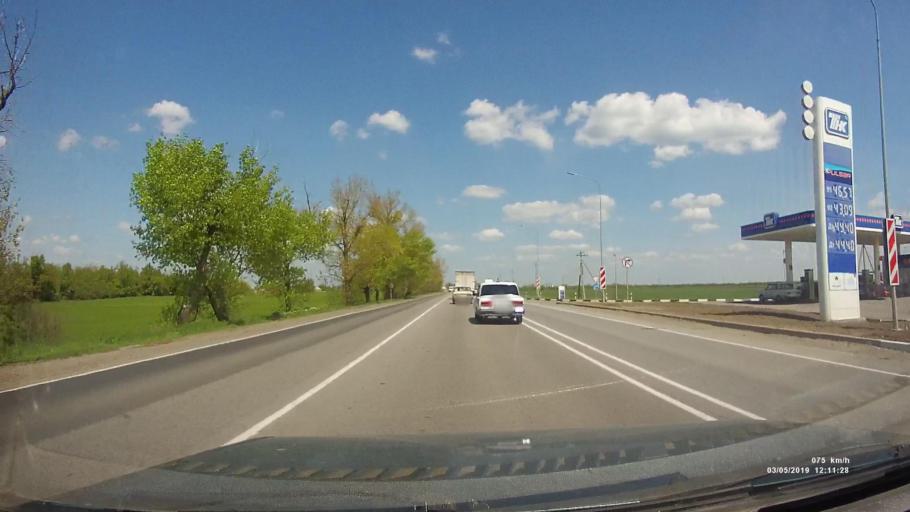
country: RU
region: Rostov
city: Bagayevskaya
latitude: 47.3114
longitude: 40.5391
